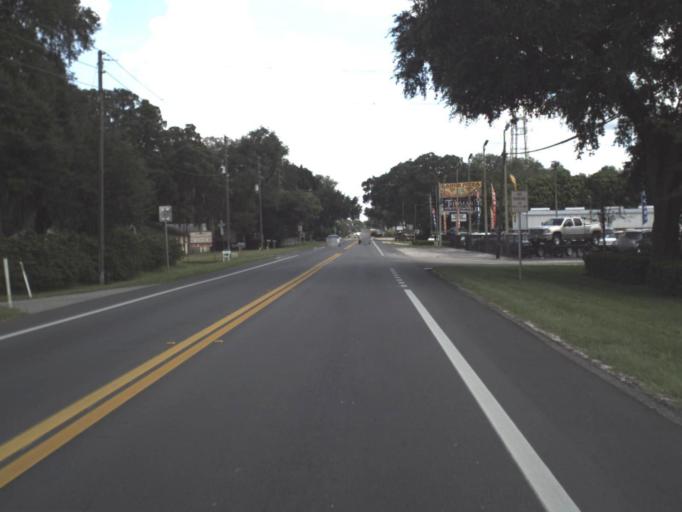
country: US
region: Florida
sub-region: Pasco County
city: Zephyrhills
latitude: 28.2232
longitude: -82.1799
